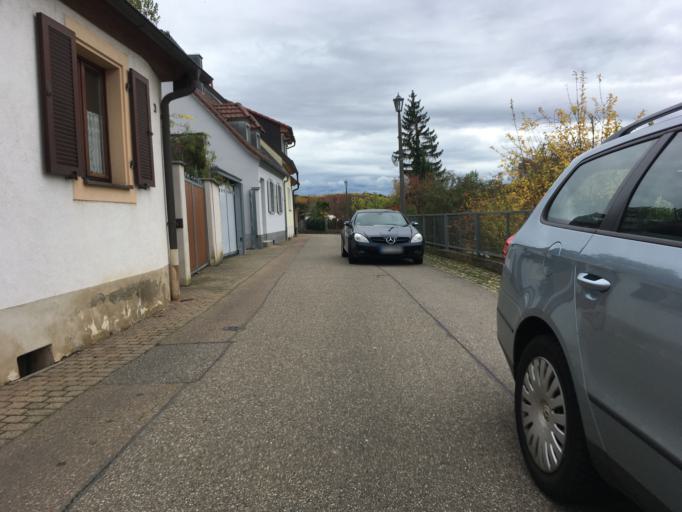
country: DE
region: Baden-Wuerttemberg
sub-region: Freiburg Region
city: Breisach am Rhein
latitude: 48.0291
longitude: 7.5782
